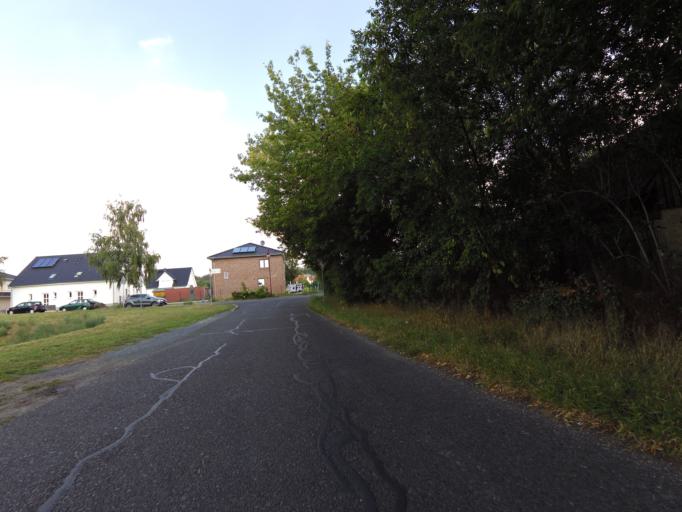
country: DE
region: Berlin
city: Lichtenrade
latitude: 52.3560
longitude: 13.3976
